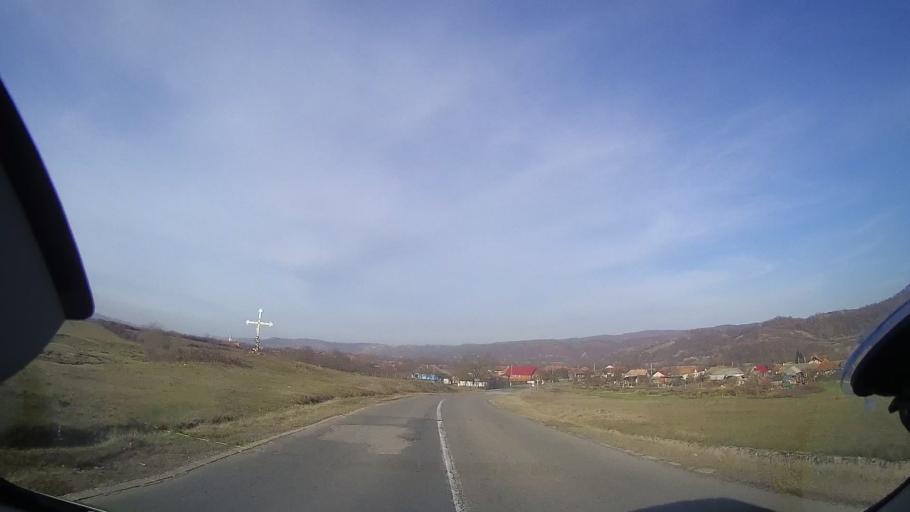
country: RO
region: Bihor
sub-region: Comuna Brusturi
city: Brusturi
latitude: 47.1346
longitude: 22.2684
